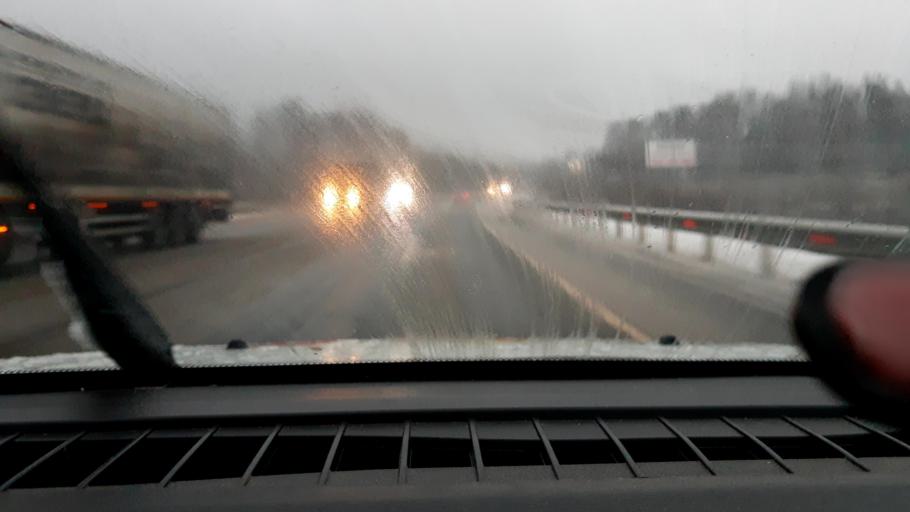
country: RU
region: Nizjnij Novgorod
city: Kstovo
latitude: 56.1583
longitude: 44.1545
